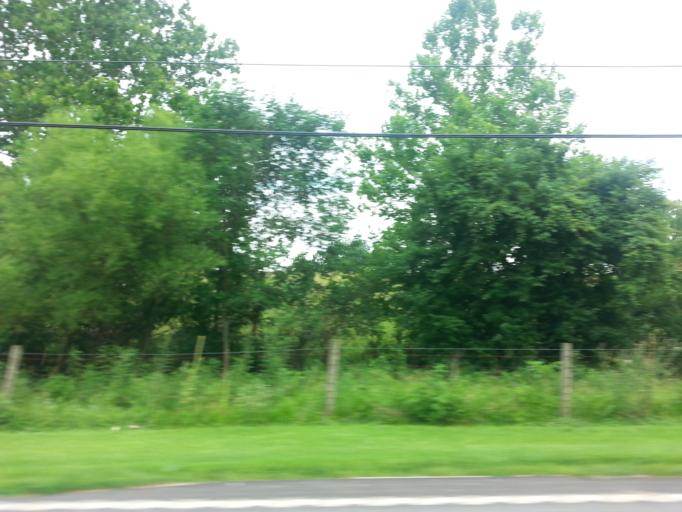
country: US
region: Kentucky
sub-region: Harrison County
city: Cynthiana
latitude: 38.4424
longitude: -84.2471
